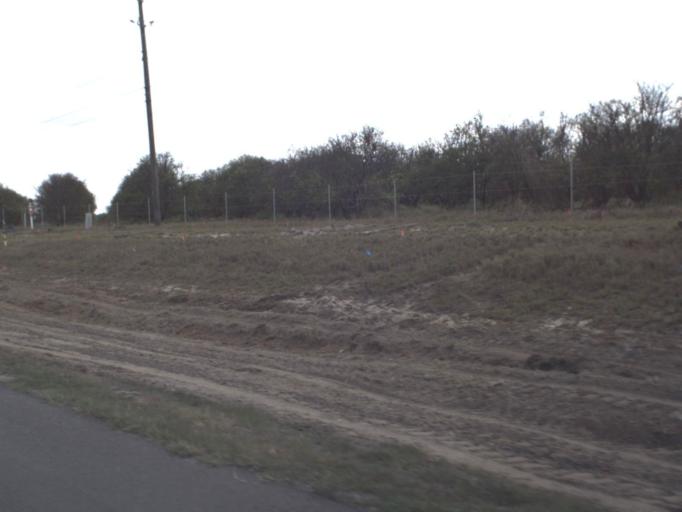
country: US
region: Florida
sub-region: Lake County
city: Four Corners
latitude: 28.4101
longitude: -81.7006
